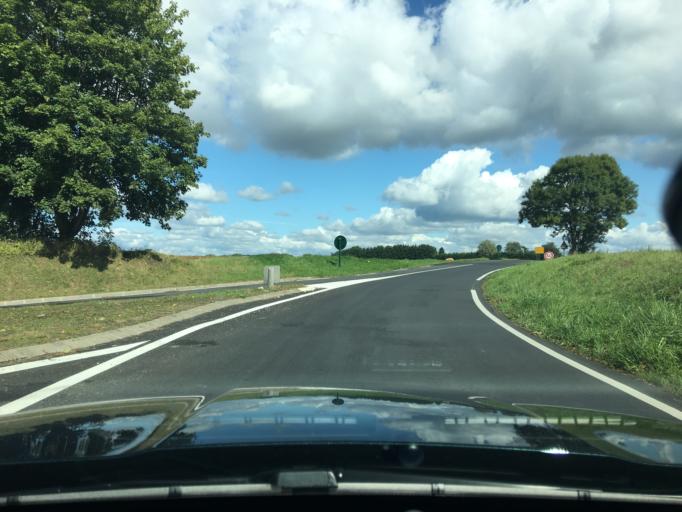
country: FR
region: Ile-de-France
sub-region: Departement du Val-d'Oise
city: Survilliers
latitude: 49.0784
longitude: 2.5294
